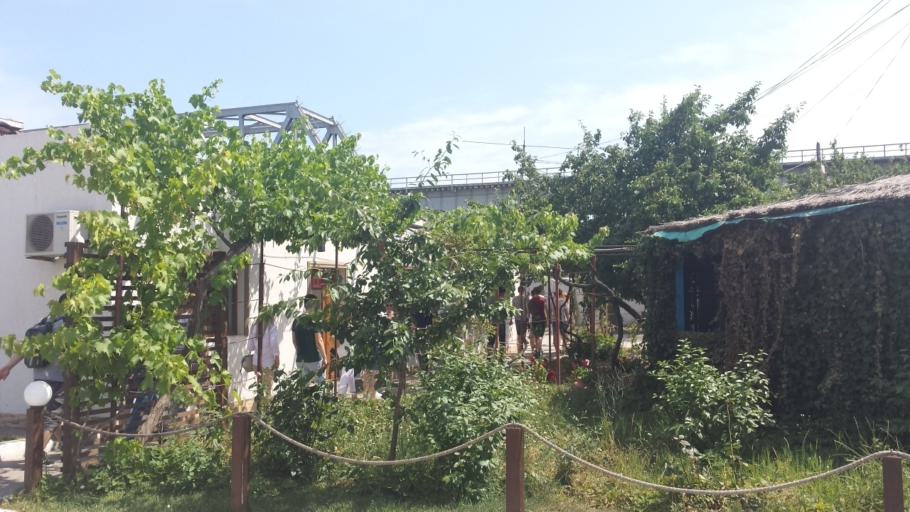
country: RO
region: Constanta
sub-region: Comuna Navodari
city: Navodari
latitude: 44.3273
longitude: 28.6200
